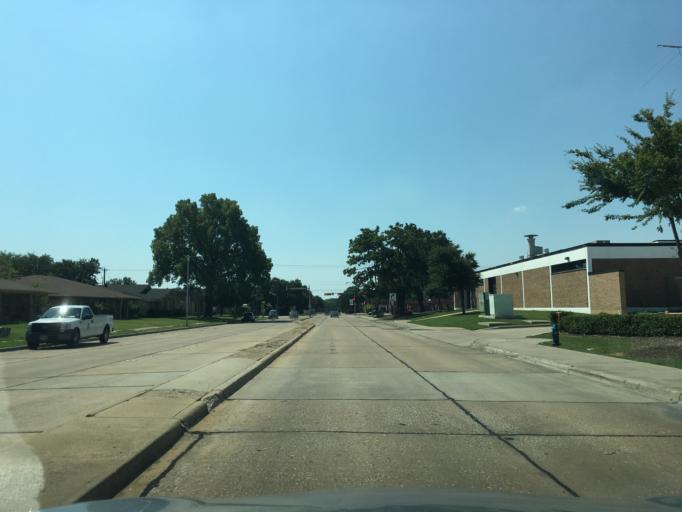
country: US
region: Texas
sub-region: Dallas County
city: Garland
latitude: 32.9319
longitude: -96.6573
